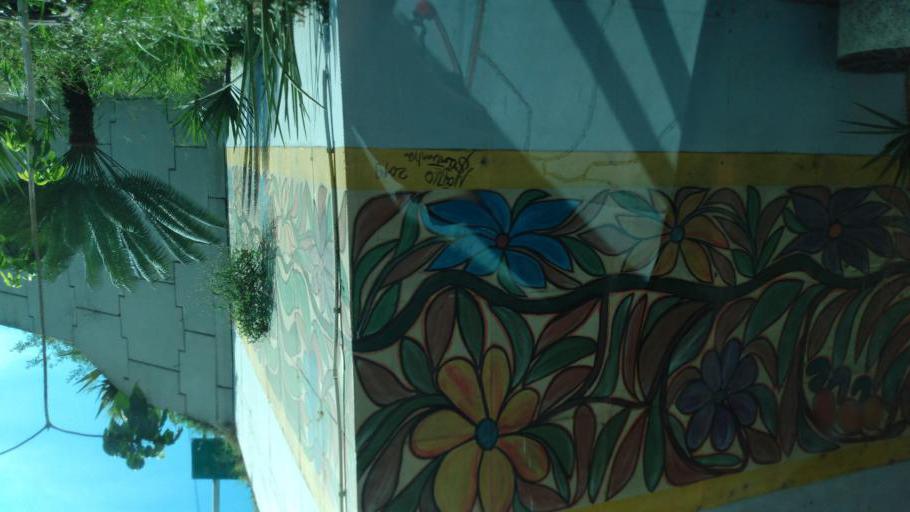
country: ET
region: Oromiya
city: Gore
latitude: 8.1946
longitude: 35.5621
